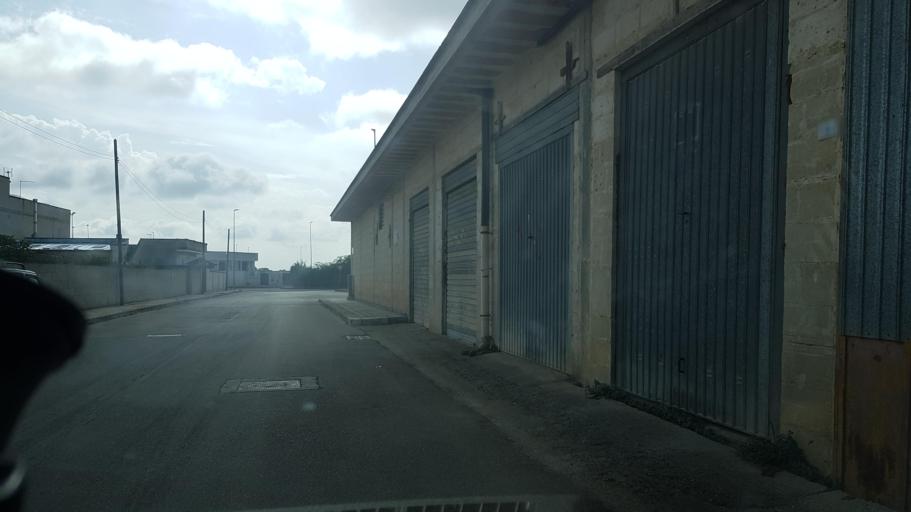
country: IT
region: Apulia
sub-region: Provincia di Brindisi
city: San Donaci
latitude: 40.4489
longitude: 17.9301
